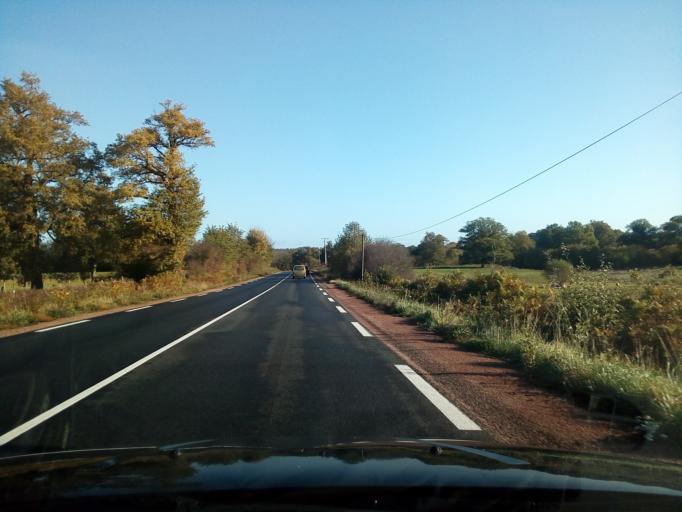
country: FR
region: Limousin
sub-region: Departement de la Haute-Vienne
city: Bellac
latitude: 46.1435
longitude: 1.0999
